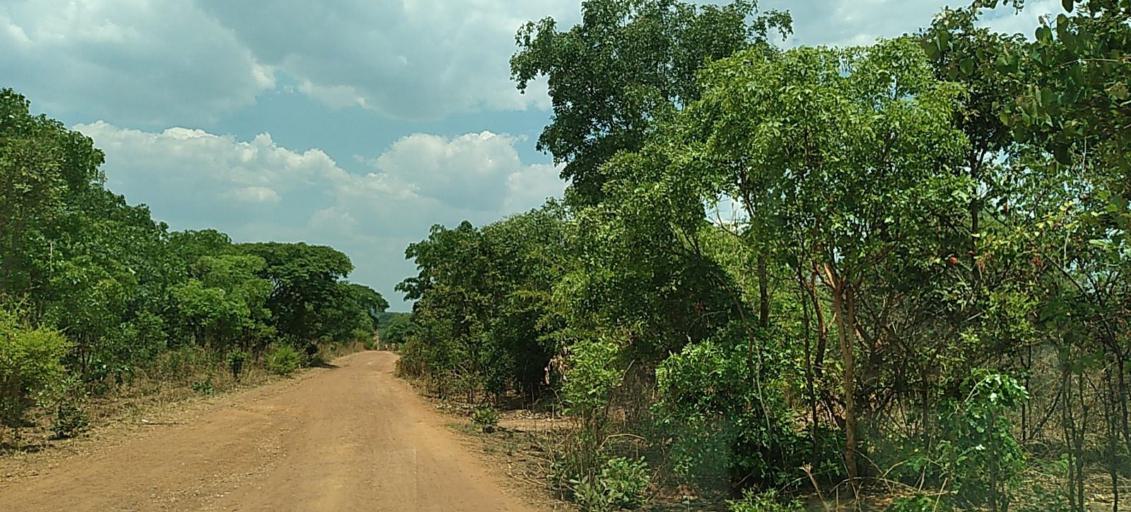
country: ZM
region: Copperbelt
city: Luanshya
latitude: -13.3871
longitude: 28.4445
